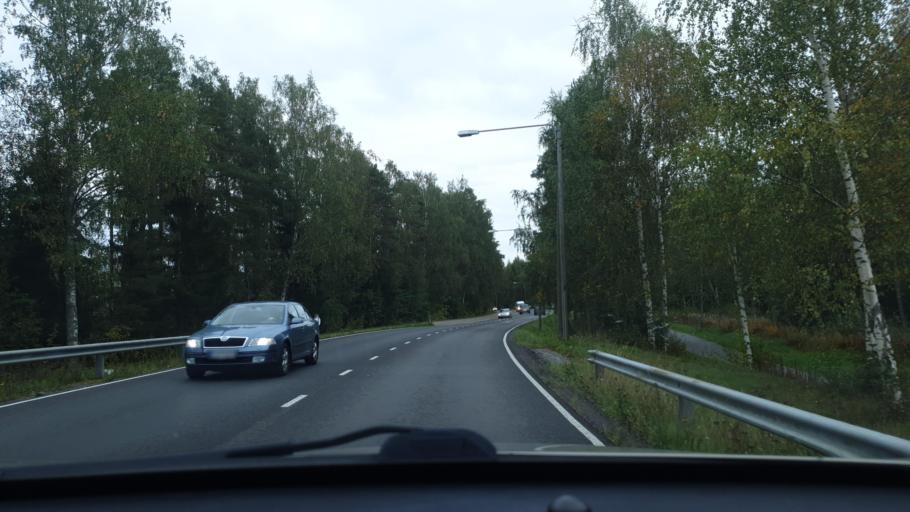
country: FI
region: Ostrobothnia
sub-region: Vaasa
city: Teeriniemi
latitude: 63.0894
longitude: 21.6901
